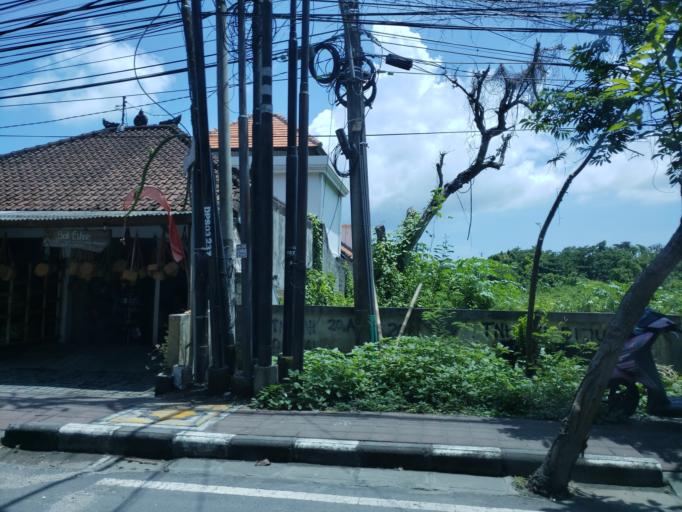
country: ID
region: Bali
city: Jimbaran
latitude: -8.7840
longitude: 115.1663
